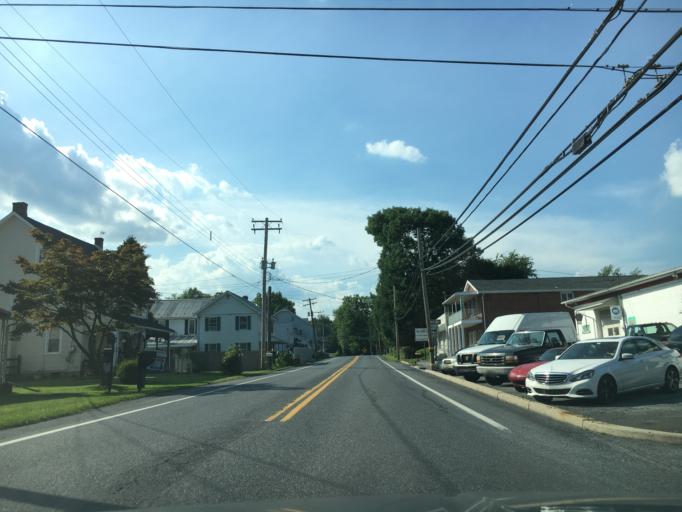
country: US
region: Pennsylvania
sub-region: Lehigh County
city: Egypt
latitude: 40.6691
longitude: -75.5668
